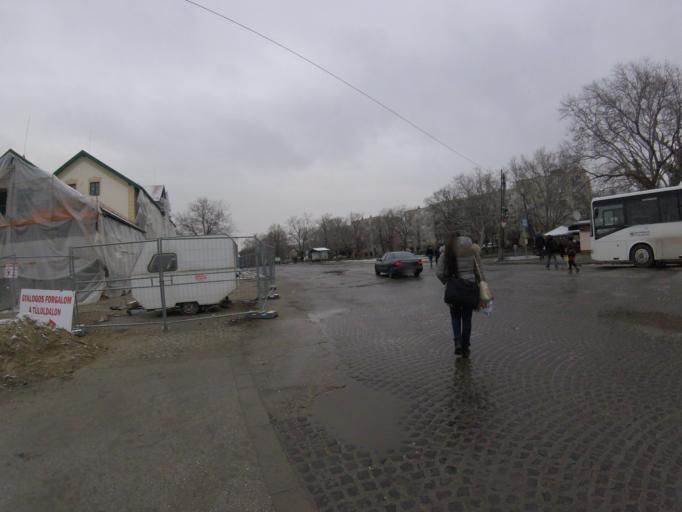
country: HU
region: Komarom-Esztergom
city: Esztergom
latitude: 47.7778
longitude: 18.7437
